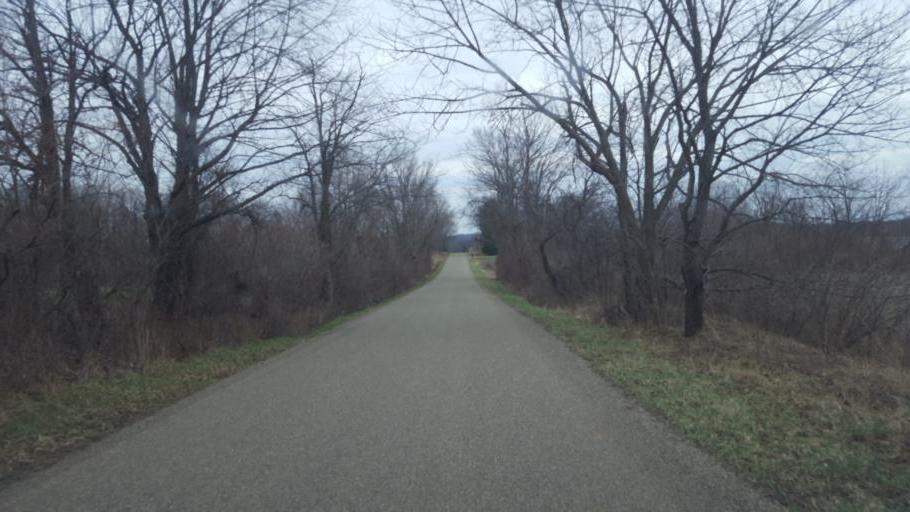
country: US
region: Ohio
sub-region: Sandusky County
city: Bellville
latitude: 40.6816
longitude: -82.4795
